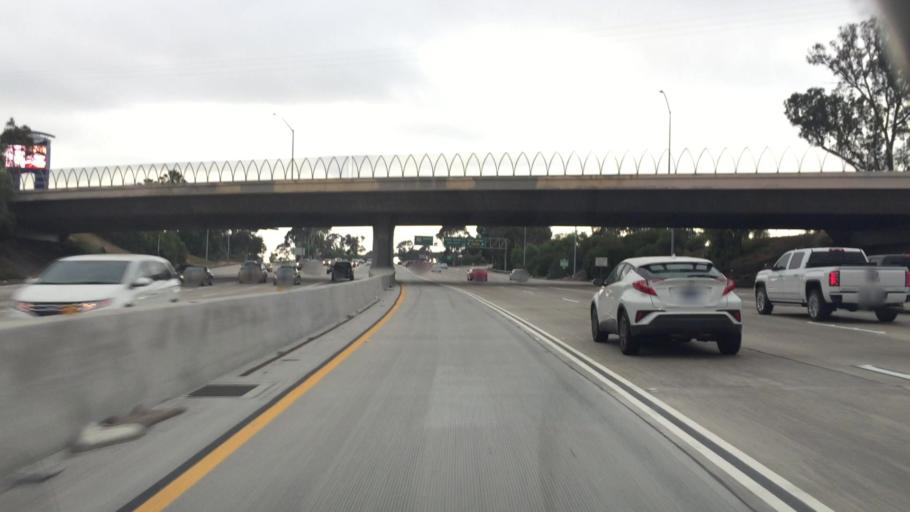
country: US
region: California
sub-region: San Diego County
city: National City
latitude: 32.6841
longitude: -117.0887
